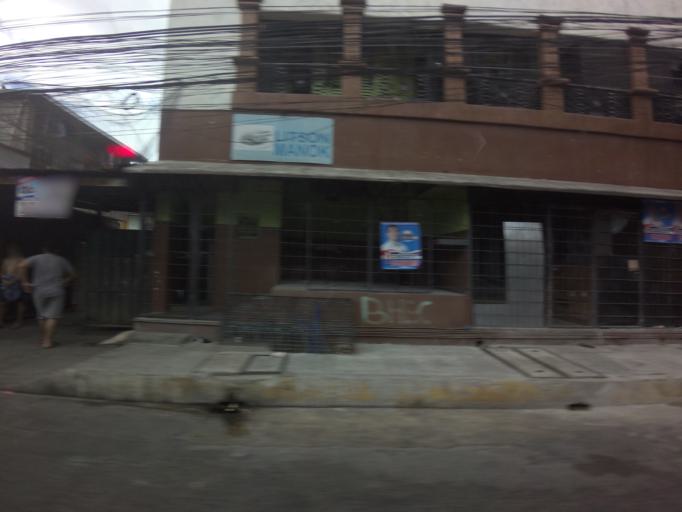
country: PH
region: Calabarzon
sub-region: Province of Rizal
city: Pateros
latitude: 14.5619
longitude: 121.0832
